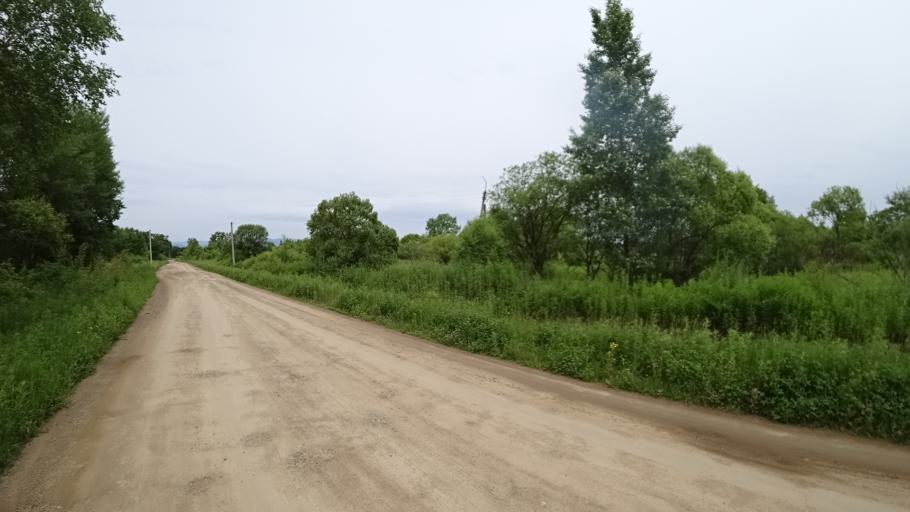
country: RU
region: Primorskiy
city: Arsen'yev
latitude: 44.1946
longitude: 133.3092
